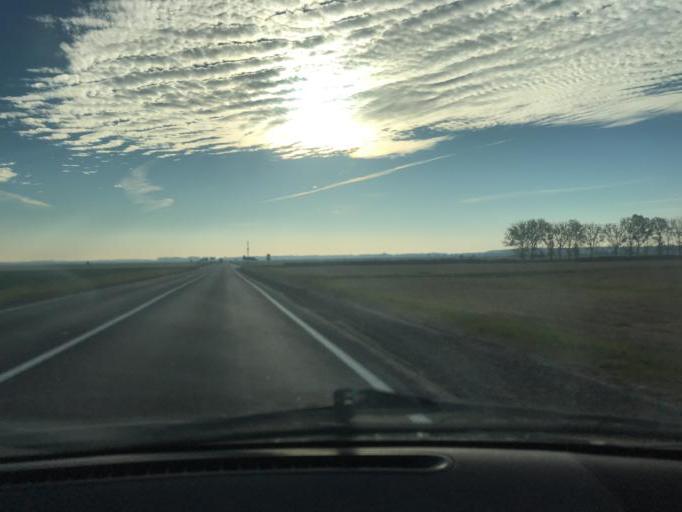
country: BY
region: Brest
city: Drahichyn
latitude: 52.2200
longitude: 25.1698
